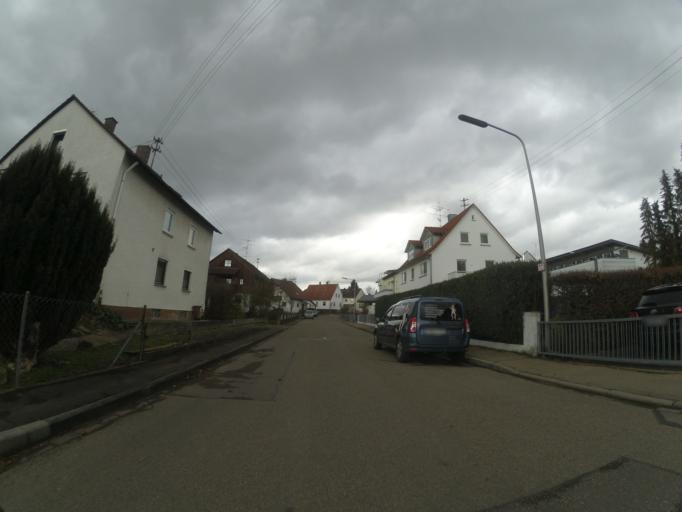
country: DE
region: Bavaria
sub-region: Swabia
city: Senden
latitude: 48.3166
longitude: 10.0742
